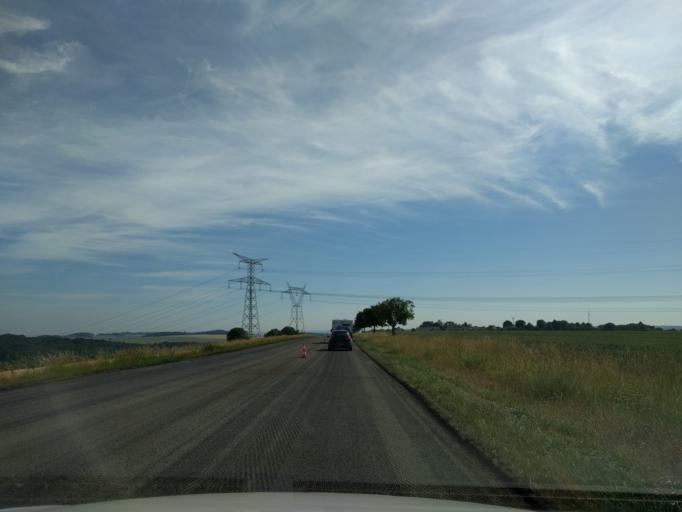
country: FR
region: Picardie
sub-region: Departement de l'Oise
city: Breteuil
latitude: 49.5750
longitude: 2.2321
